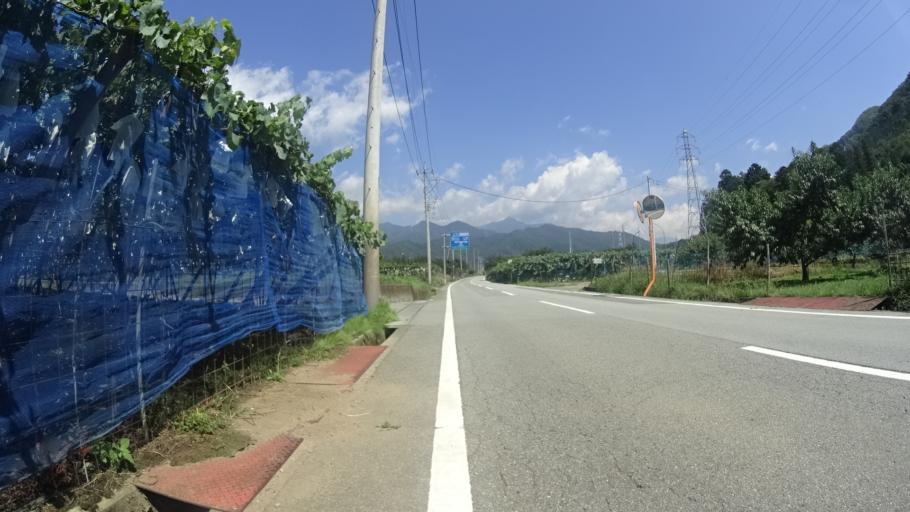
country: JP
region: Yamanashi
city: Enzan
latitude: 35.7363
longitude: 138.7216
